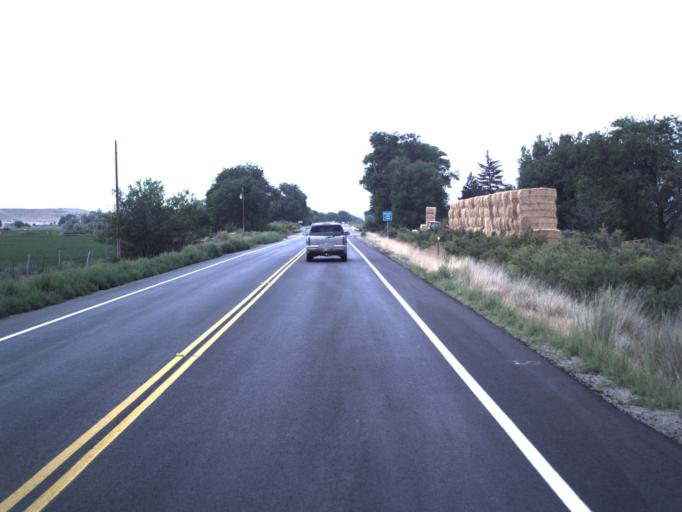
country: US
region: Utah
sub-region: Duchesne County
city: Duchesne
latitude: 40.1552
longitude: -110.2040
